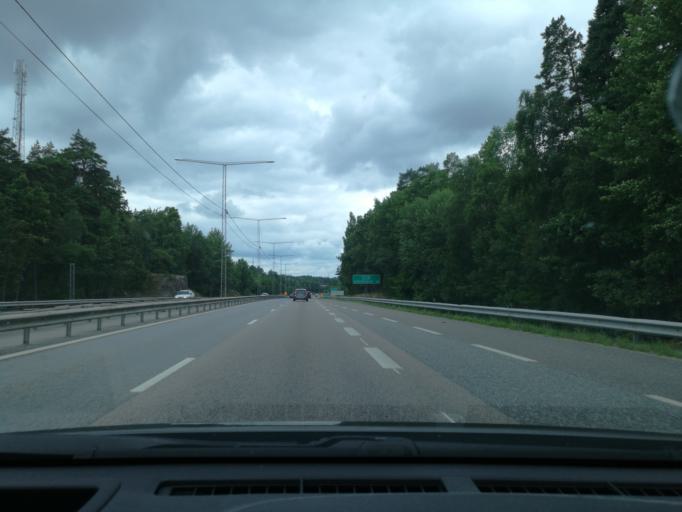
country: SE
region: Stockholm
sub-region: Taby Kommun
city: Taby
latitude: 59.4413
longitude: 18.0905
